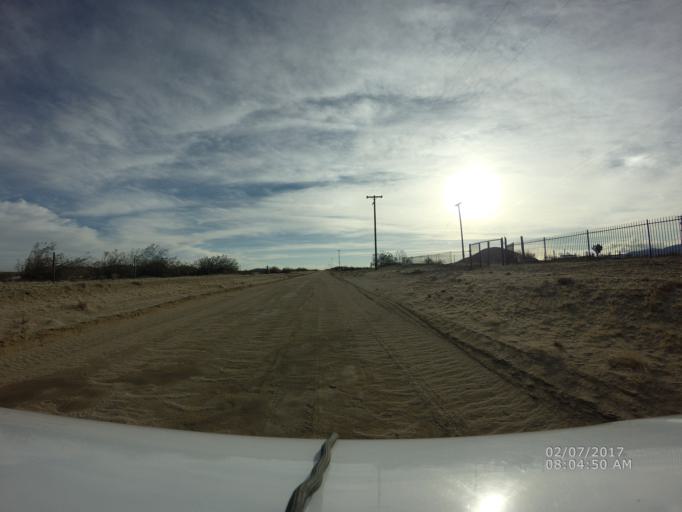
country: US
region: California
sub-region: Los Angeles County
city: Lake Los Angeles
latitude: 34.5725
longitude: -117.7518
